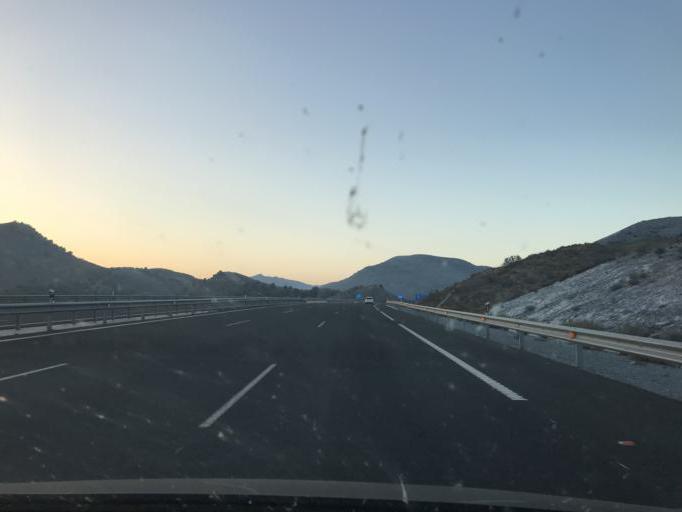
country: ES
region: Andalusia
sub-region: Provincia de Granada
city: Motril
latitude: 36.7773
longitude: -3.4990
